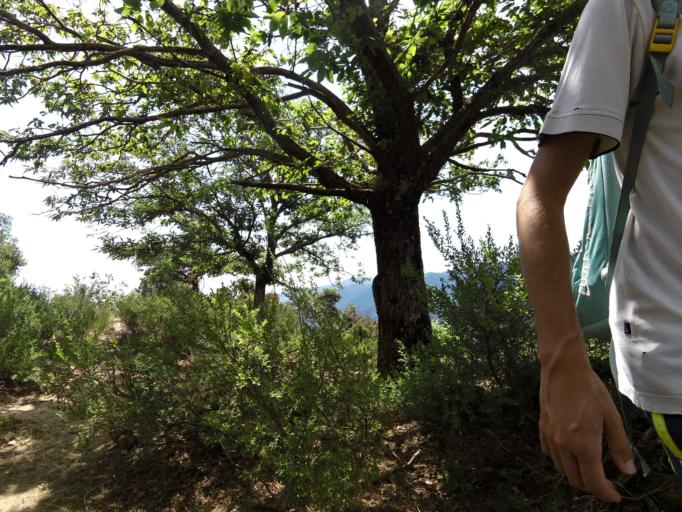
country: IT
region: Calabria
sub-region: Provincia di Reggio Calabria
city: Bivongi
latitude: 38.5081
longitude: 16.3958
